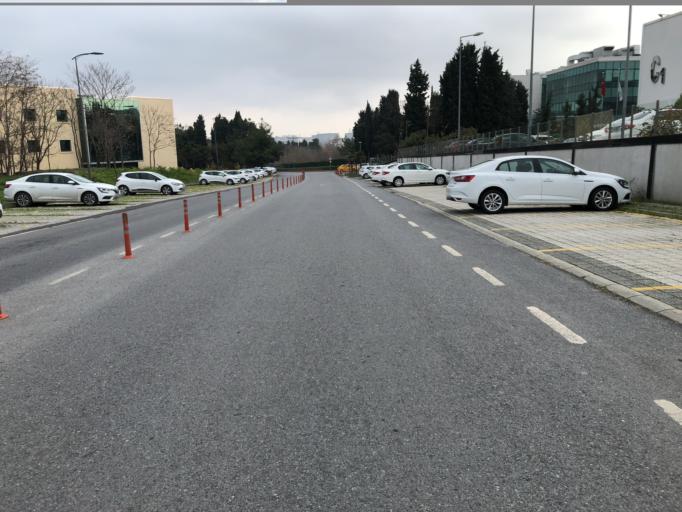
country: TR
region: Istanbul
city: merter keresteciler
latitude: 41.0208
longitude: 28.8896
